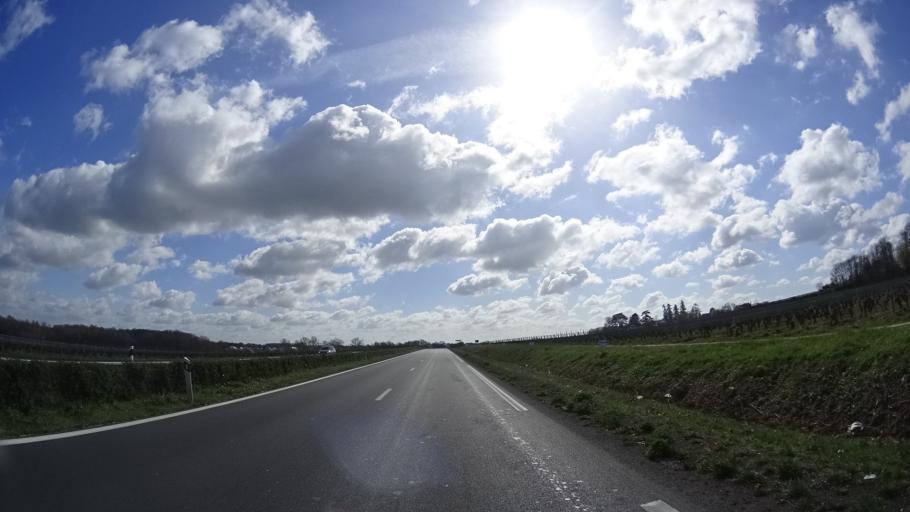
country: FR
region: Pays de la Loire
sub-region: Departement de Maine-et-Loire
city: Juigne-sur-Loire
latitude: 47.3827
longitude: -0.4800
